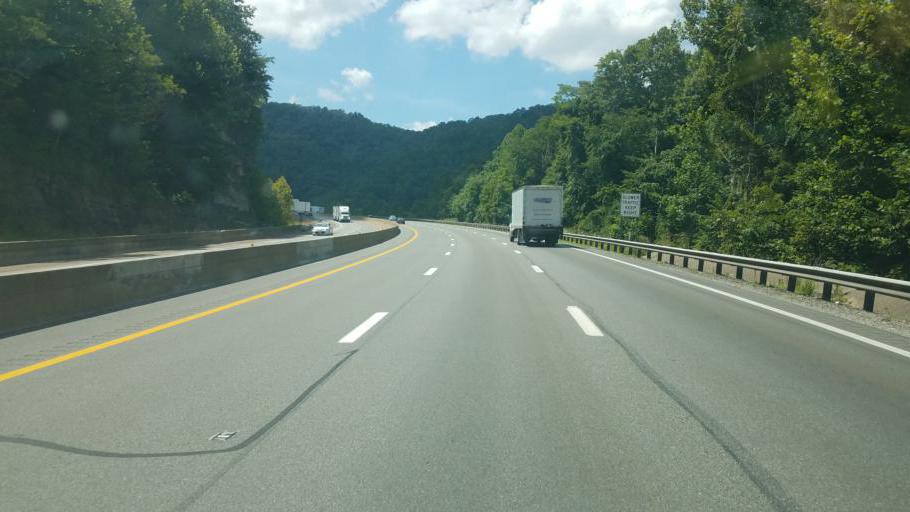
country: US
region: West Virginia
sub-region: Kanawha County
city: Montgomery
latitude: 38.1340
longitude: -81.4010
